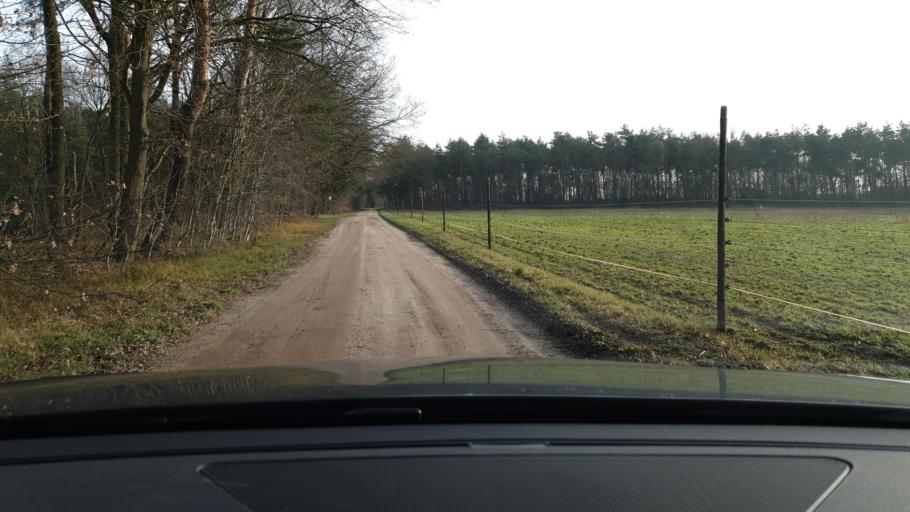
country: NL
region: Limburg
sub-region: Gemeente Peel en Maas
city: Maasbree
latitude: 51.4366
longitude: 6.0689
